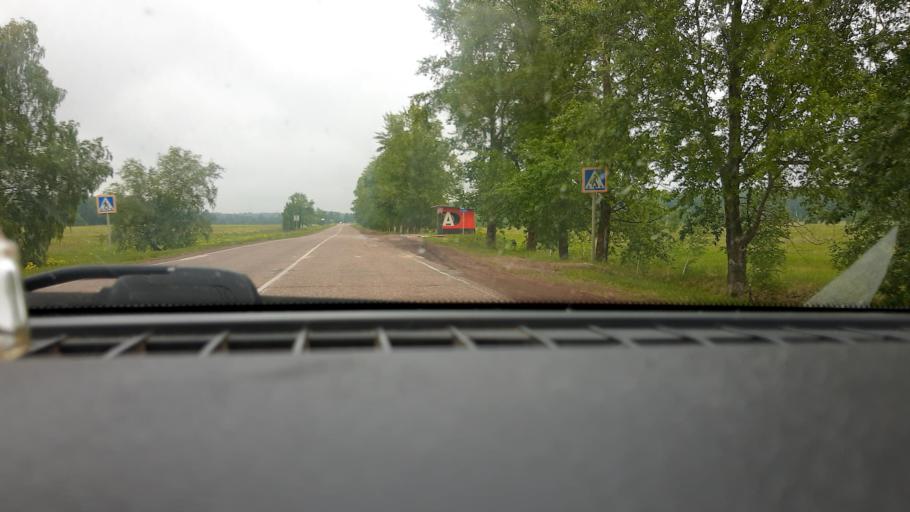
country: RU
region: Bashkortostan
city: Belebey
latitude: 54.0666
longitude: 54.0623
